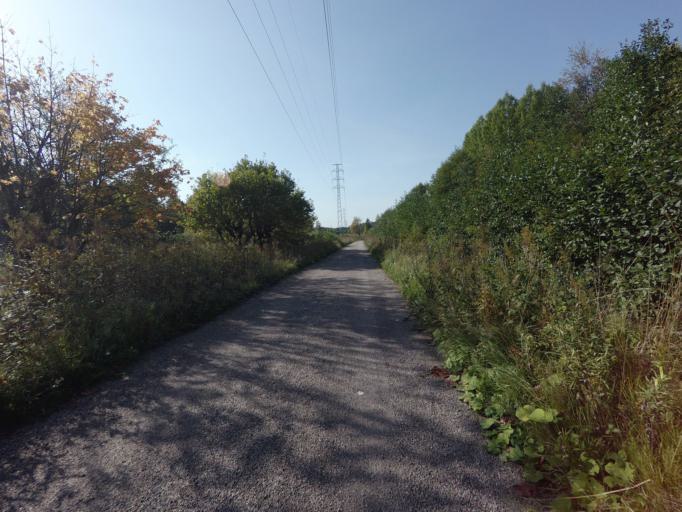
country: FI
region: Uusimaa
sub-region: Helsinki
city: Kauniainen
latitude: 60.1804
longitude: 24.7109
